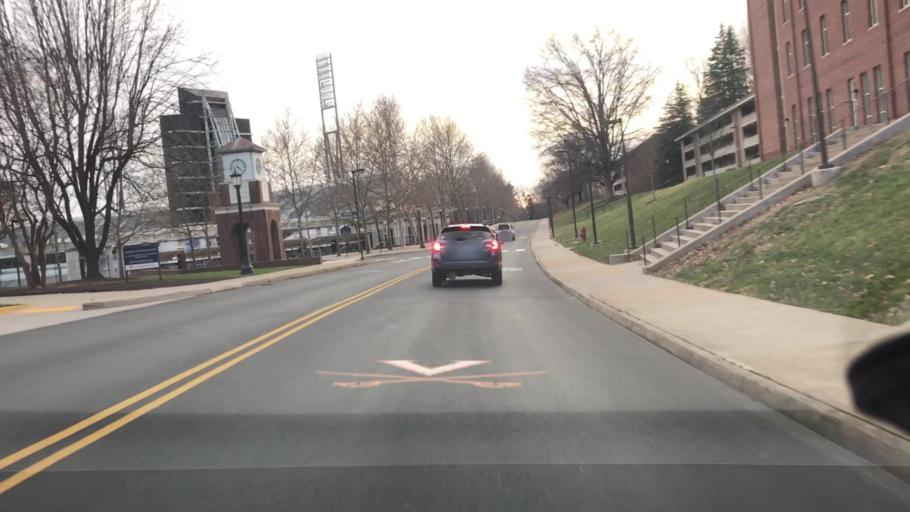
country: US
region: Virginia
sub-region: City of Charlottesville
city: Charlottesville
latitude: 38.0331
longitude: -78.5144
